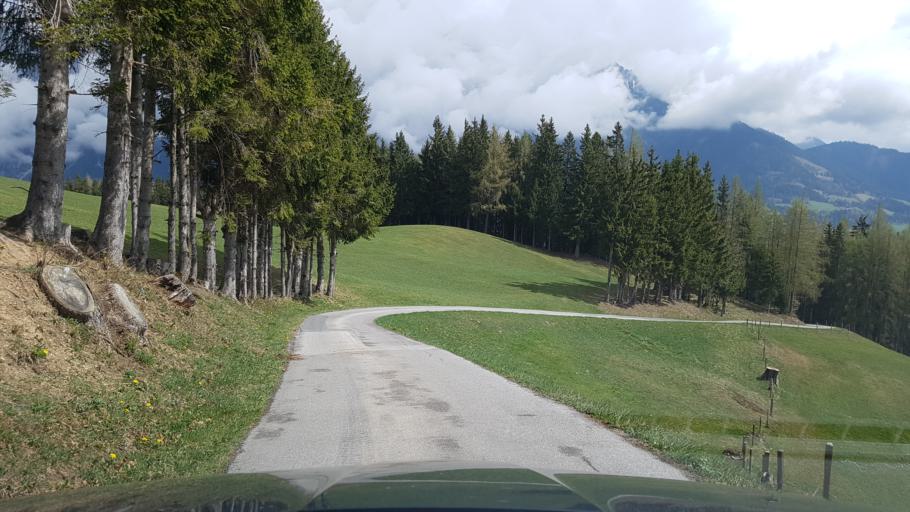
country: AT
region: Salzburg
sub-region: Politischer Bezirk Sankt Johann im Pongau
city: Werfen
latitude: 47.4601
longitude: 13.1741
